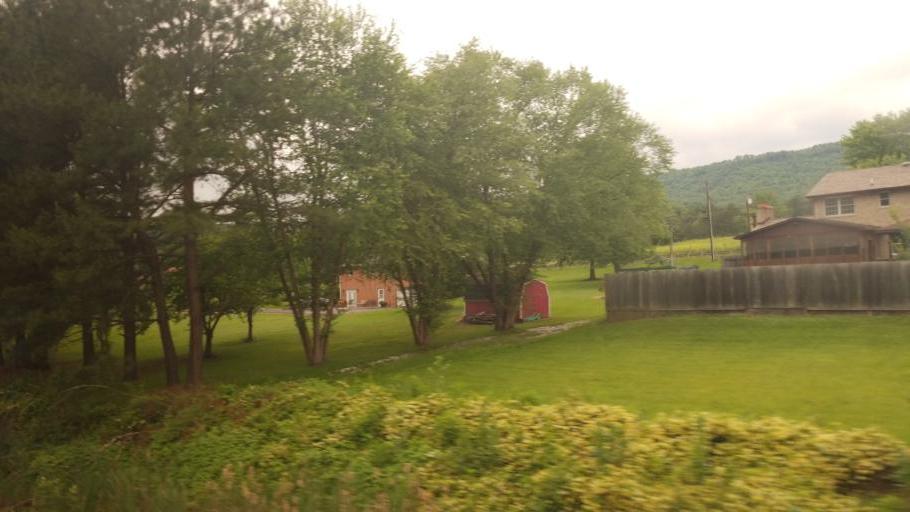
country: US
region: Maryland
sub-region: Allegany County
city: Cumberland
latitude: 39.7040
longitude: -78.7823
